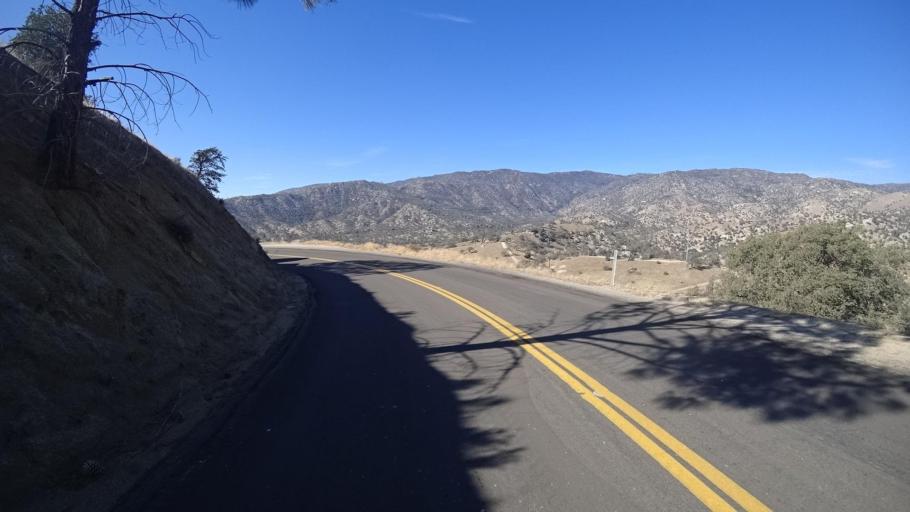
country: US
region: California
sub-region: Kern County
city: Bodfish
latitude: 35.5948
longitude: -118.5116
